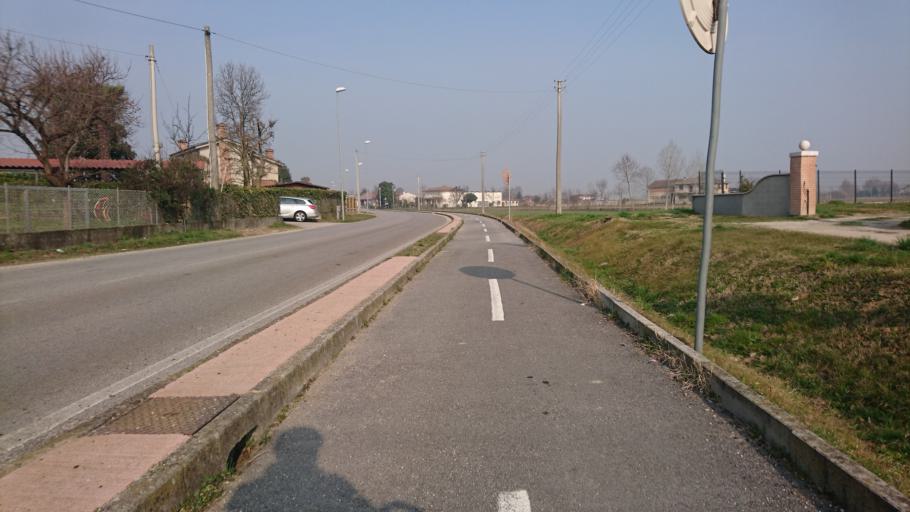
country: IT
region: Veneto
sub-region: Provincia di Padova
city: Veggiano
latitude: 45.4517
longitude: 11.7060
